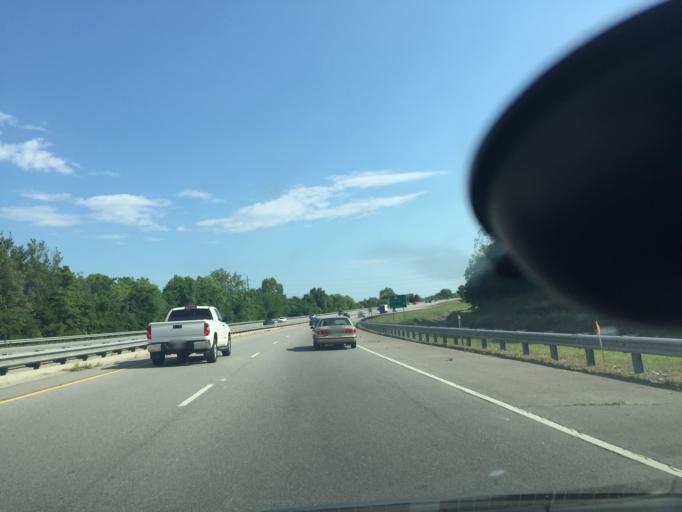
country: US
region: Georgia
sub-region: Chatham County
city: Thunderbolt
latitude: 32.0499
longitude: -81.0691
